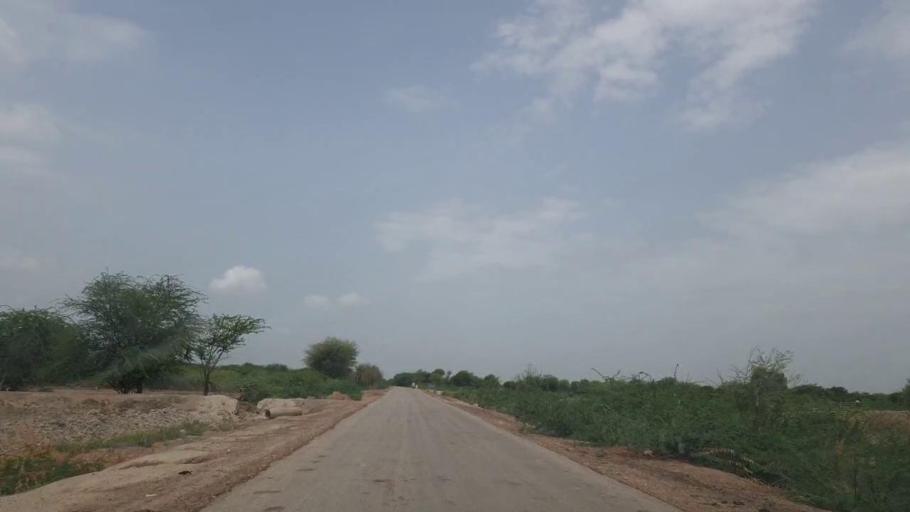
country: PK
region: Sindh
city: Digri
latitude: 24.9393
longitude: 69.1589
